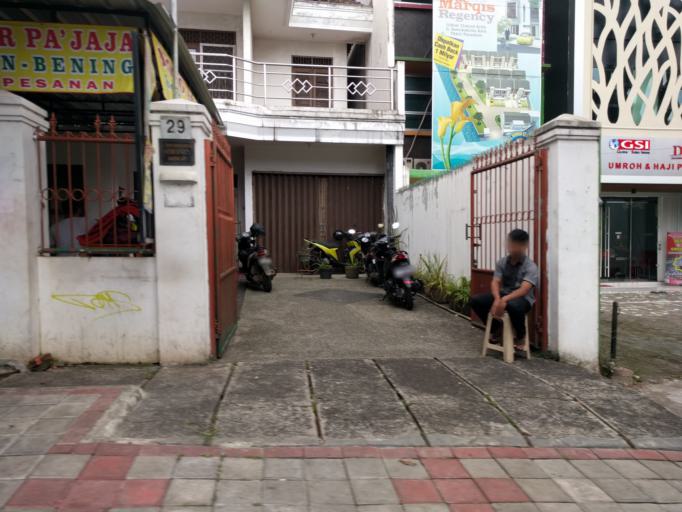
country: ID
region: West Java
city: Bogor
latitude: -6.5810
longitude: 106.8101
